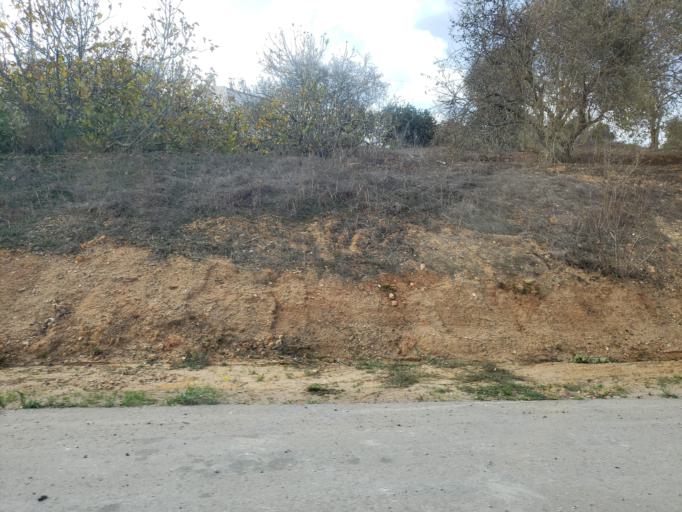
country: PT
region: Faro
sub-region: Portimao
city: Portimao
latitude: 37.1583
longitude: -8.5630
